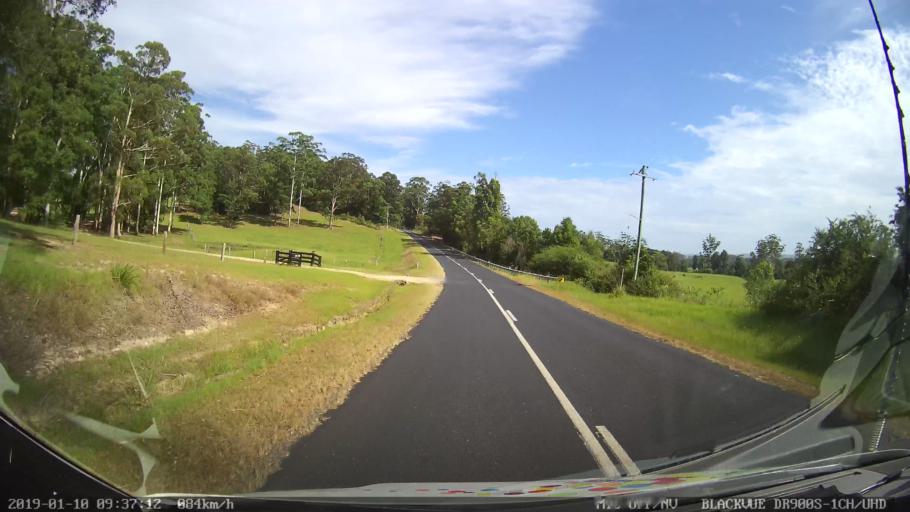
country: AU
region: New South Wales
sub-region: Coffs Harbour
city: Nana Glen
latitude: -30.1902
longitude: 153.0115
